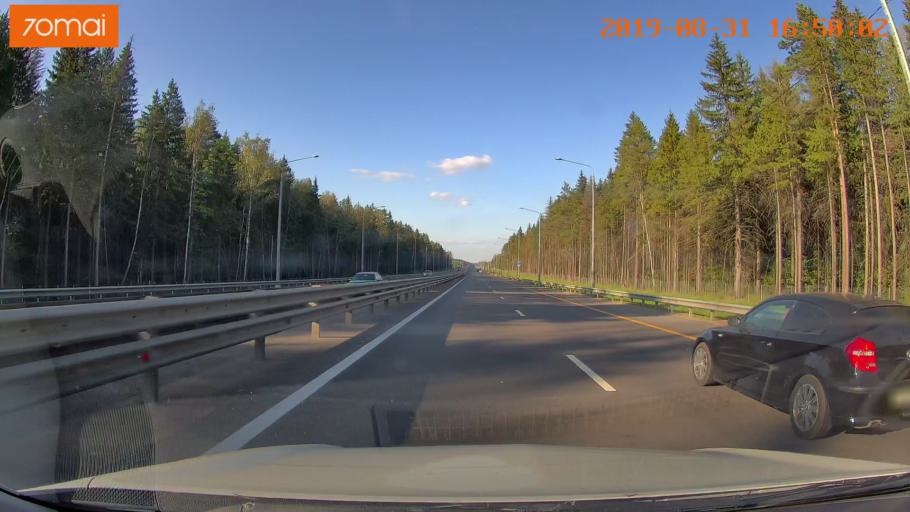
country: RU
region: Kaluga
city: Pyatovskiy
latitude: 54.7012
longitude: 36.1594
